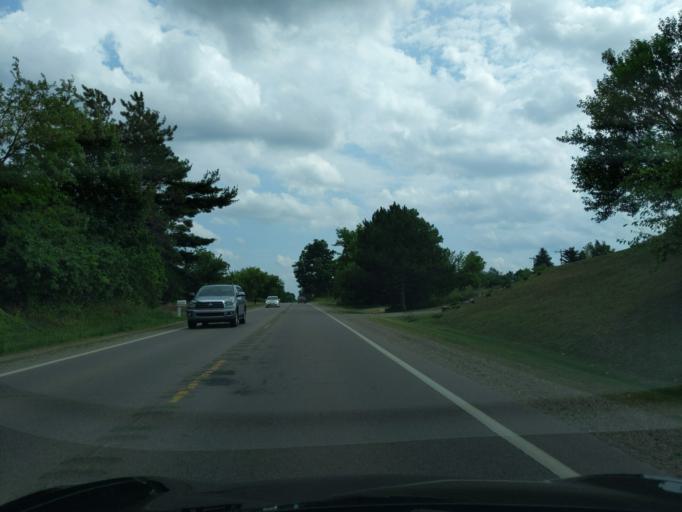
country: US
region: Michigan
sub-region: Eaton County
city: Eaton Rapids
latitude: 42.4826
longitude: -84.6598
